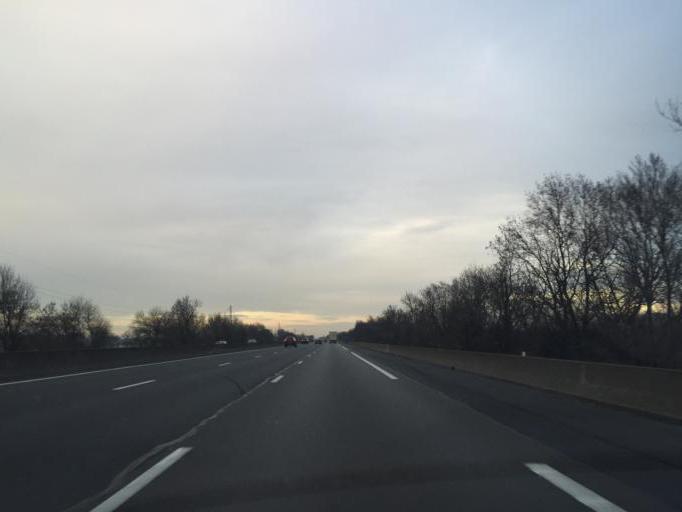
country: FR
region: Bourgogne
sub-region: Departement de Saone-et-Loire
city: La Chapelle-de-Guinchay
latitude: 46.2134
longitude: 4.7857
